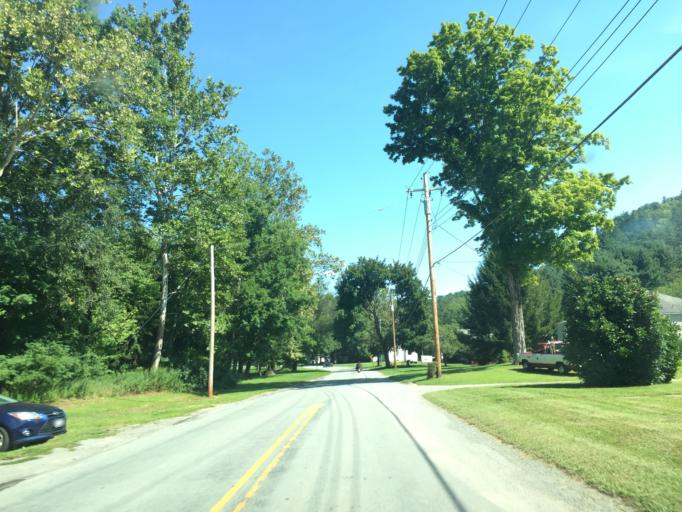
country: US
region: New York
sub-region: Sullivan County
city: Livingston Manor
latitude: 41.7607
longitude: -75.0314
